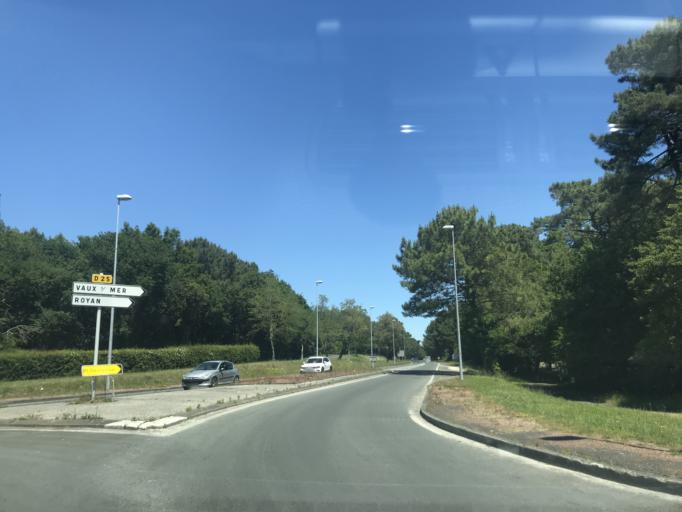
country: FR
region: Poitou-Charentes
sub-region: Departement de la Charente-Maritime
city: Saint-Palais-sur-Mer
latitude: 45.6572
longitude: -1.0892
